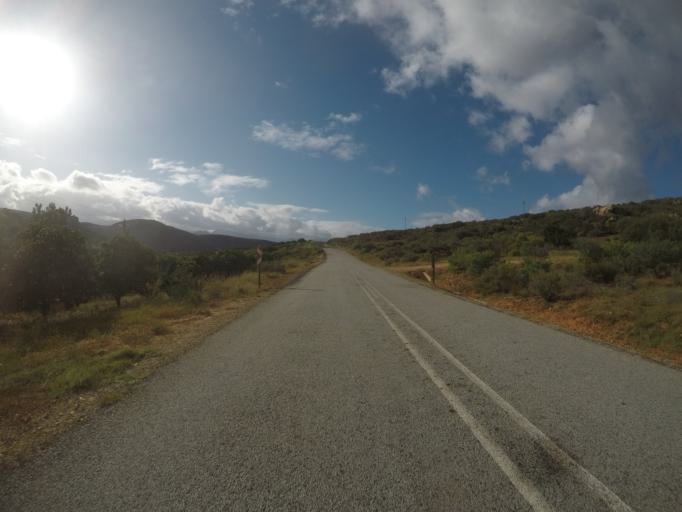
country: ZA
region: Western Cape
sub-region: West Coast District Municipality
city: Clanwilliam
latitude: -32.4206
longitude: 18.9310
